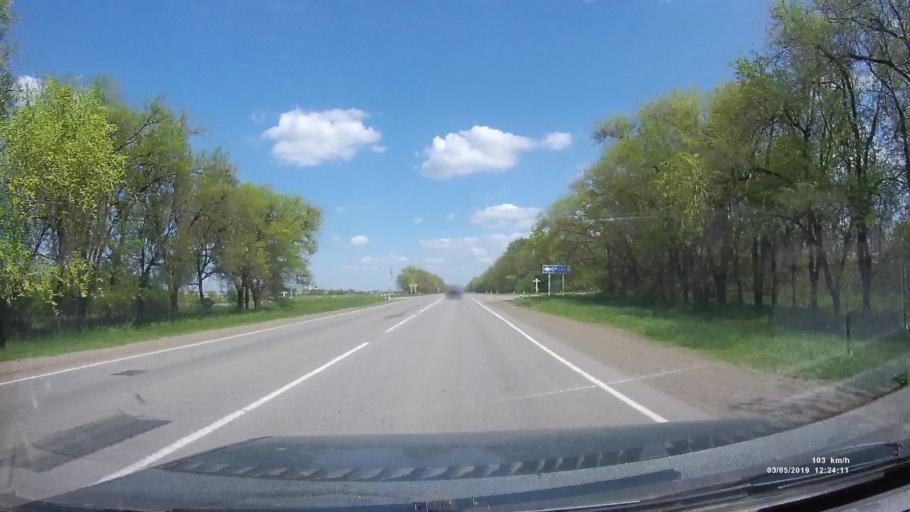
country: RU
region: Rostov
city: Semikarakorsk
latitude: 47.4173
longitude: 40.6949
